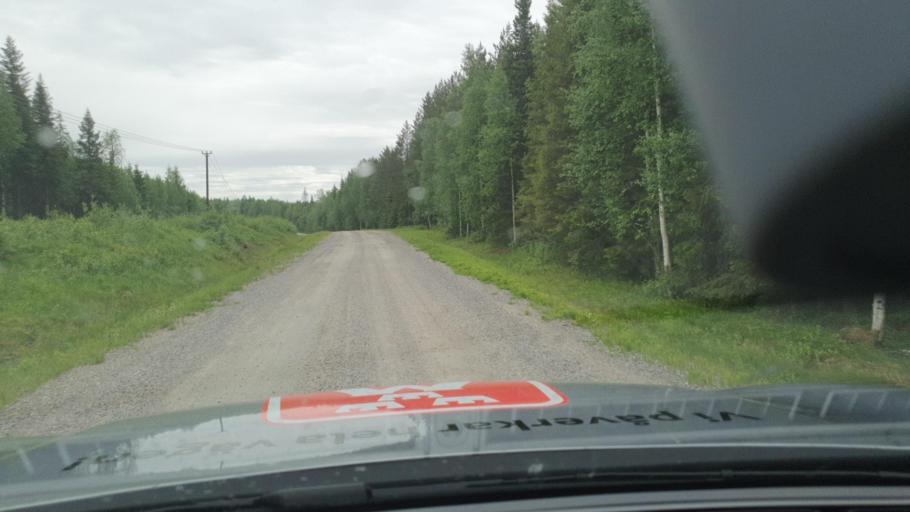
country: SE
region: Norrbotten
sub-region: Kalix Kommun
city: Rolfs
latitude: 66.0527
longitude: 23.0279
